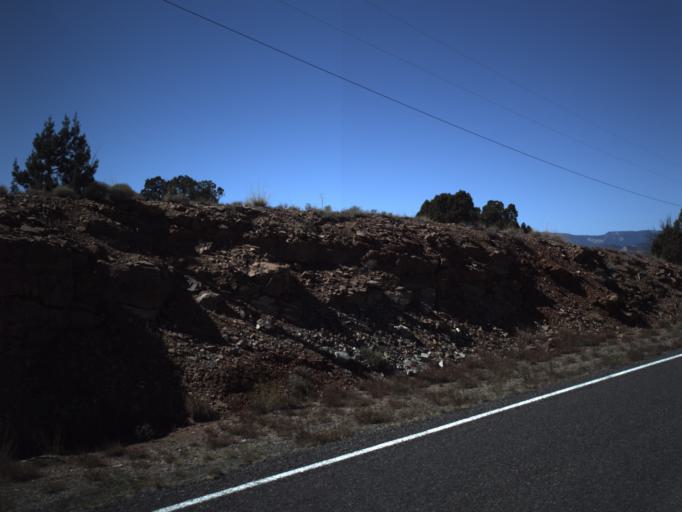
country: US
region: Utah
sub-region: Wayne County
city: Loa
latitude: 37.7291
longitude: -111.5341
